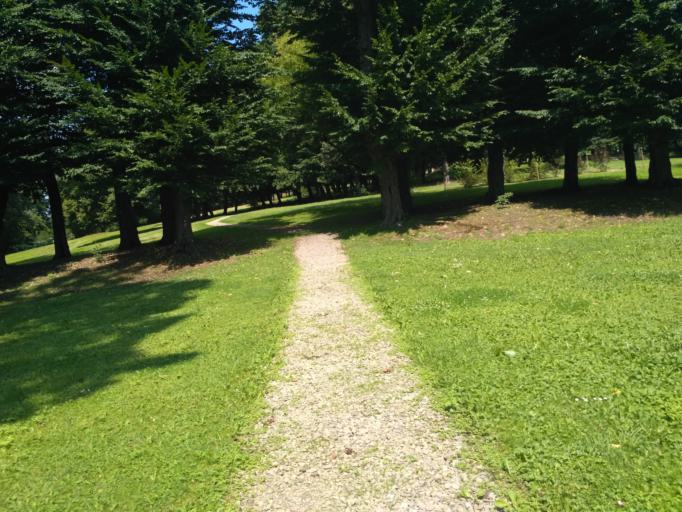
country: PL
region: Subcarpathian Voivodeship
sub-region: Powiat strzyzowski
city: Wisniowa
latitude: 49.8673
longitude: 21.6447
